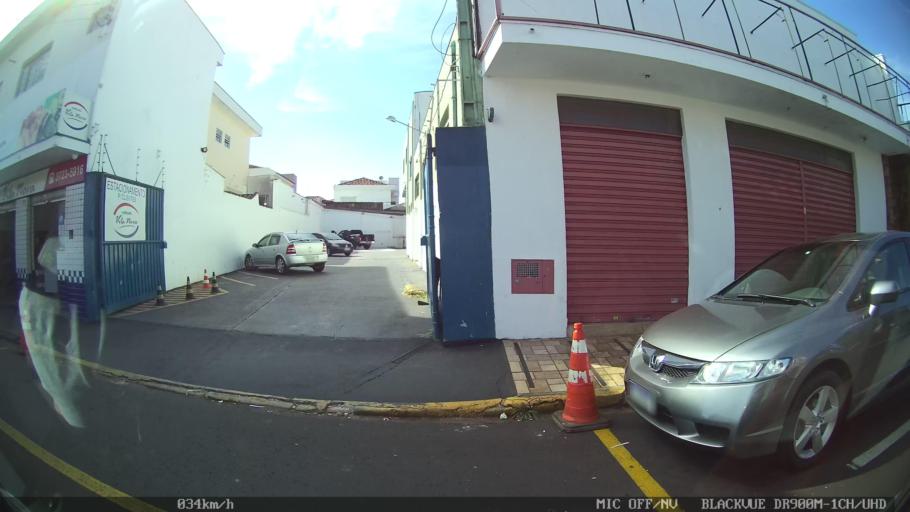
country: BR
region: Sao Paulo
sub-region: Franca
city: Franca
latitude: -20.5327
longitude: -47.4171
